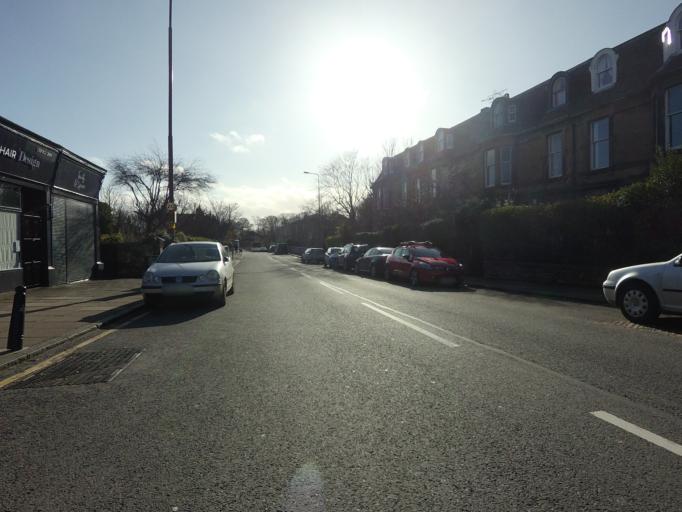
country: GB
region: Scotland
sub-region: Edinburgh
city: Edinburgh
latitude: 55.9791
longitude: -3.1930
